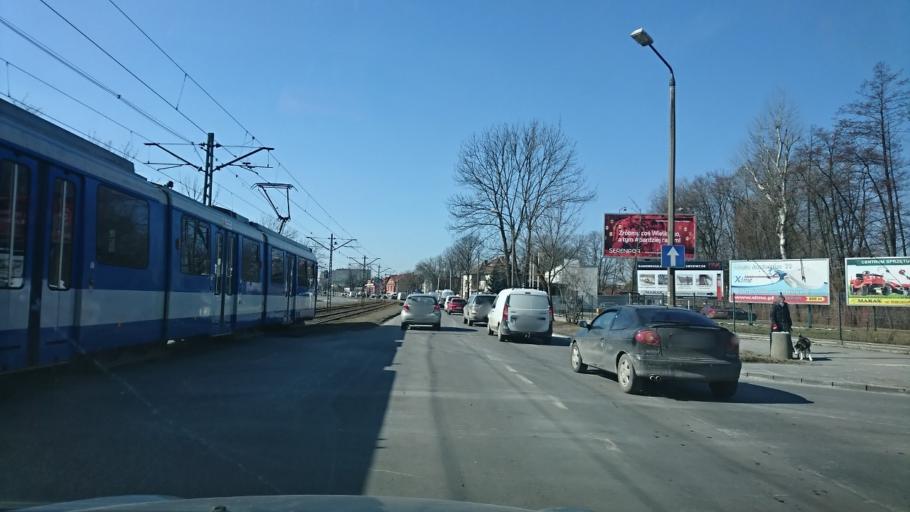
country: PL
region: Lesser Poland Voivodeship
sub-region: Powiat wielicki
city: Kokotow
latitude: 50.0863
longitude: 20.0411
